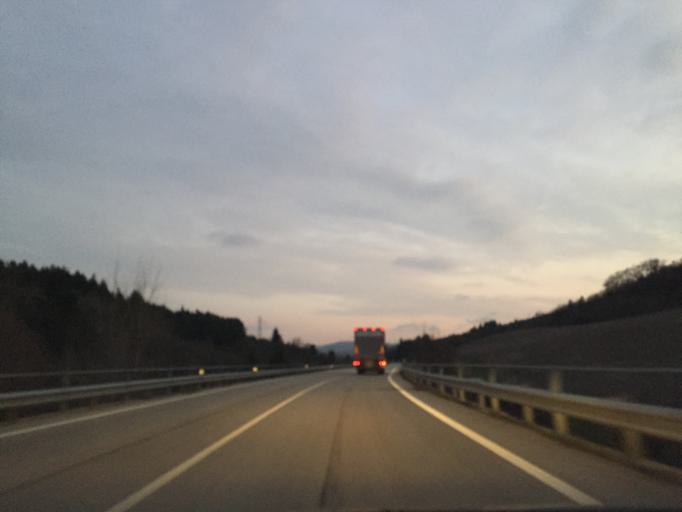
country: IT
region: Apulia
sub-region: Provincia di Foggia
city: Volturara Appula
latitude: 41.4798
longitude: 15.0534
